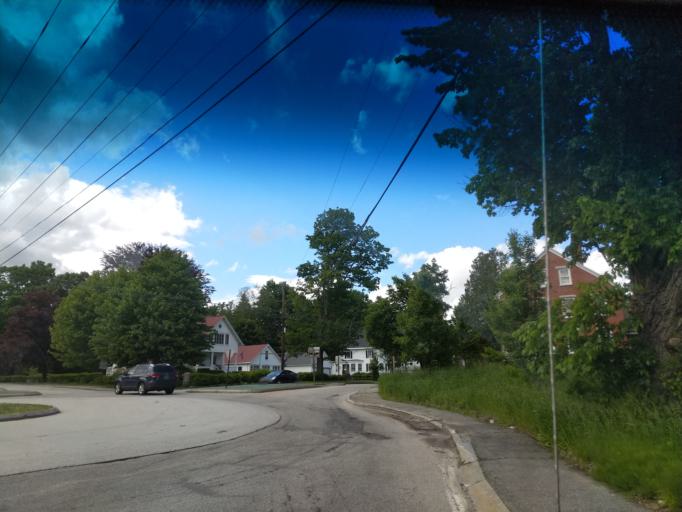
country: US
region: Maine
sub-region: Cumberland County
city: South Windham
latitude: 43.7283
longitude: -70.4250
